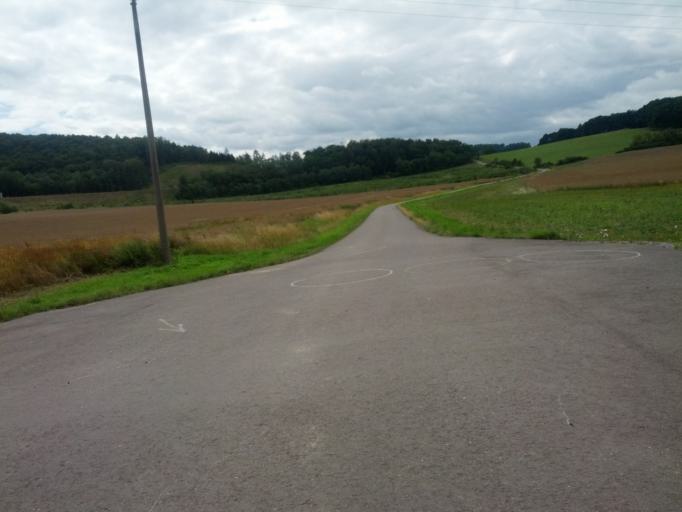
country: DE
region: Thuringia
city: Krauthausen
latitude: 51.0135
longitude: 10.2864
